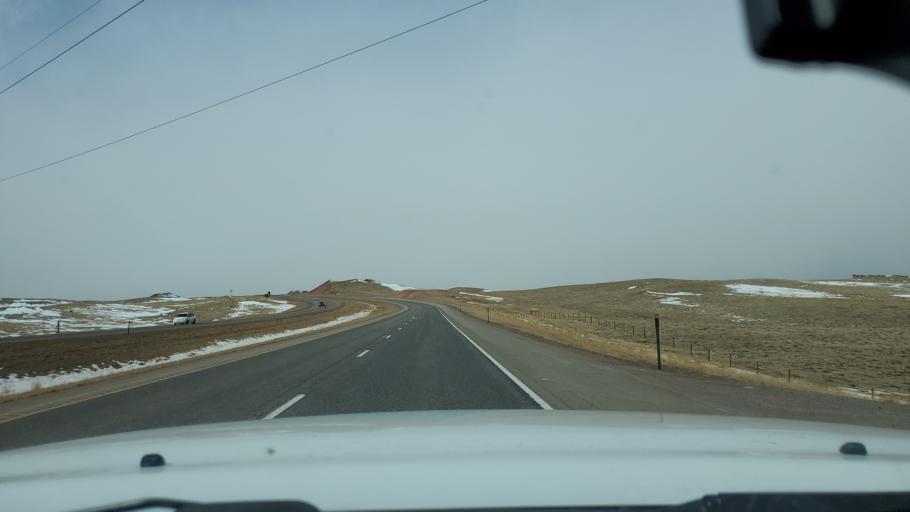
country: US
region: Wyoming
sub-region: Albany County
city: Laramie
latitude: 41.0373
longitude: -105.4458
